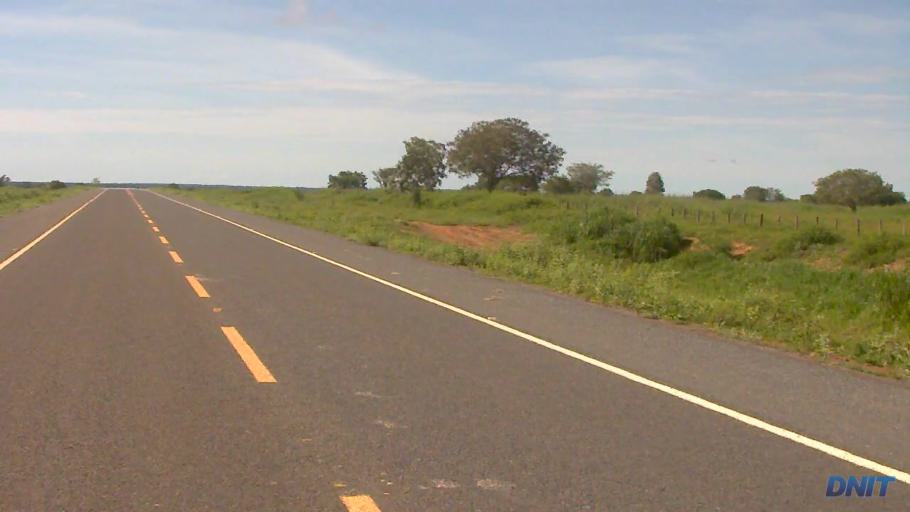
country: BR
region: Goias
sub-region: Sao Miguel Do Araguaia
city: Sao Miguel do Araguaia
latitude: -13.4802
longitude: -50.1121
